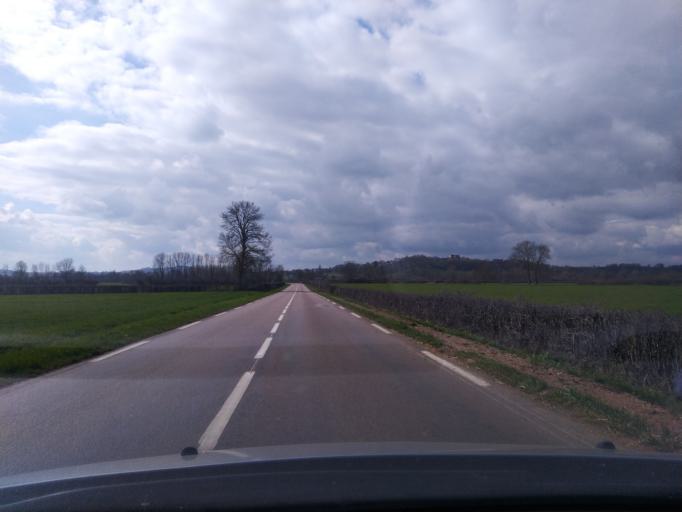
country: FR
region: Bourgogne
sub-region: Departement de l'Yonne
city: Avallon
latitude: 47.5497
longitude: 4.0548
